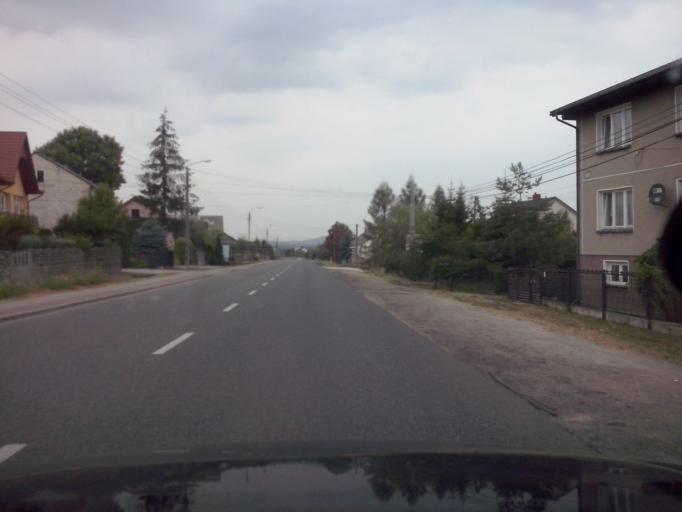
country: PL
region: Swietokrzyskie
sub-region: Powiat kielecki
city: Brzeziny
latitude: 50.7775
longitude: 20.5589
